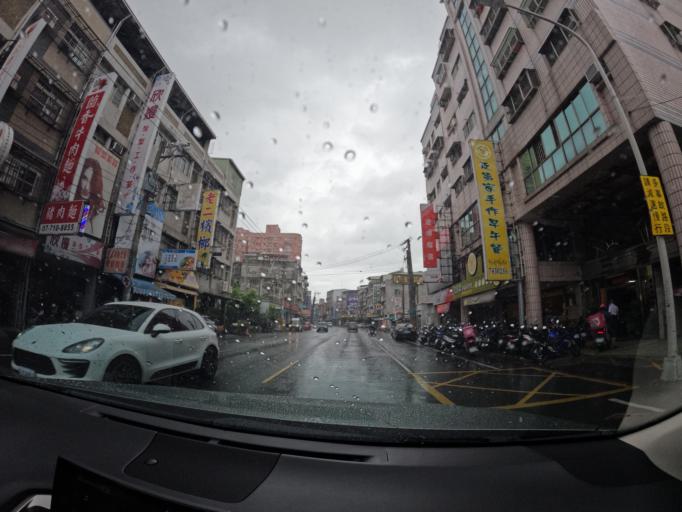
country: TW
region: Taiwan
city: Fengshan
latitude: 22.6382
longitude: 120.3645
